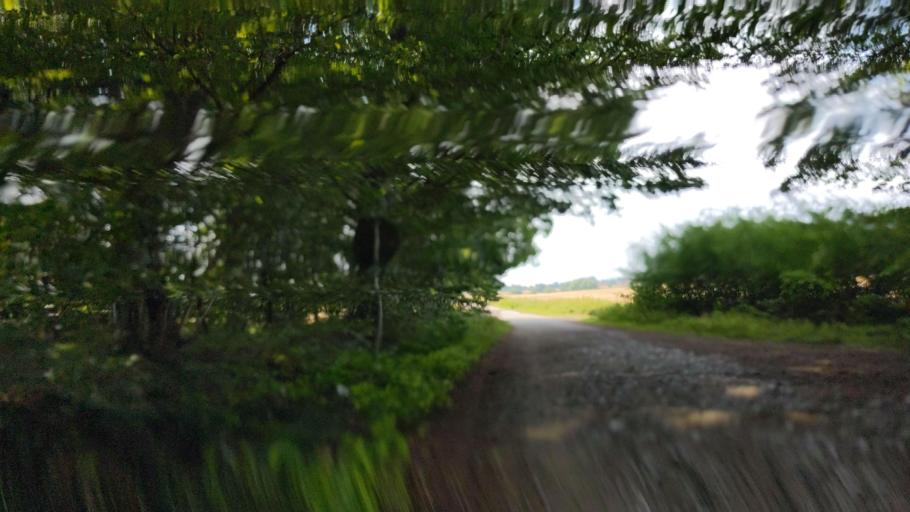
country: DE
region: Schleswig-Holstein
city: Albsfelde
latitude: 53.6916
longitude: 10.6843
